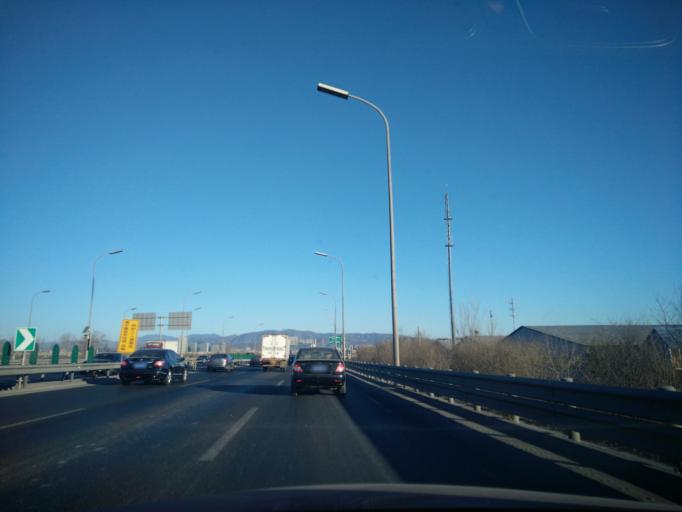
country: CN
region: Beijing
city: Lugu
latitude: 39.8712
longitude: 116.2032
